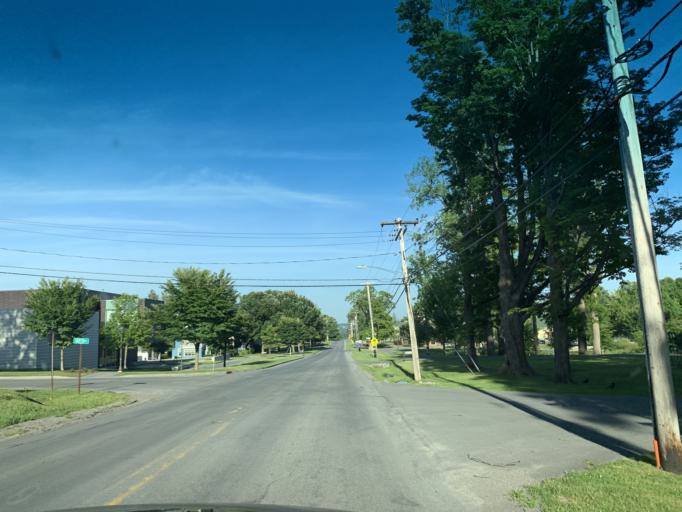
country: US
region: New York
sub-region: Oneida County
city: Clinton
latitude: 43.0508
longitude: -75.4106
